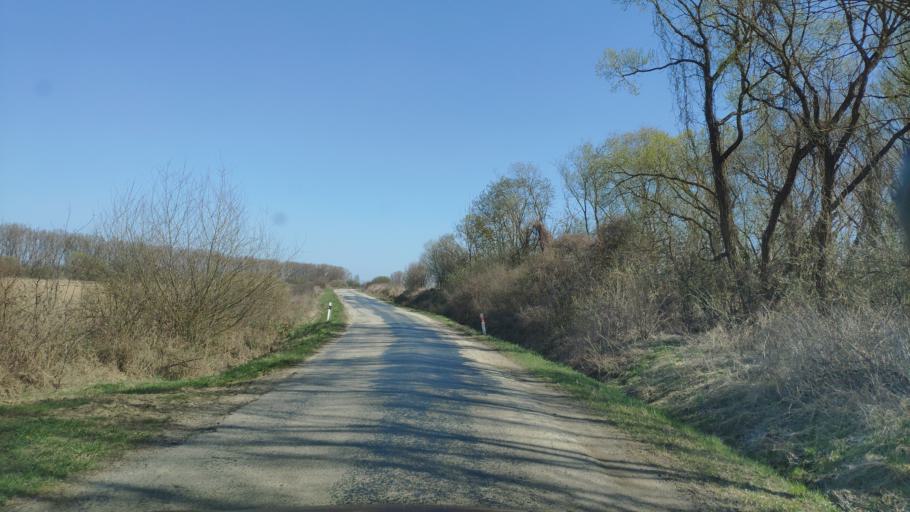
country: SK
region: Kosicky
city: Moldava nad Bodvou
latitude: 48.5634
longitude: 20.9466
